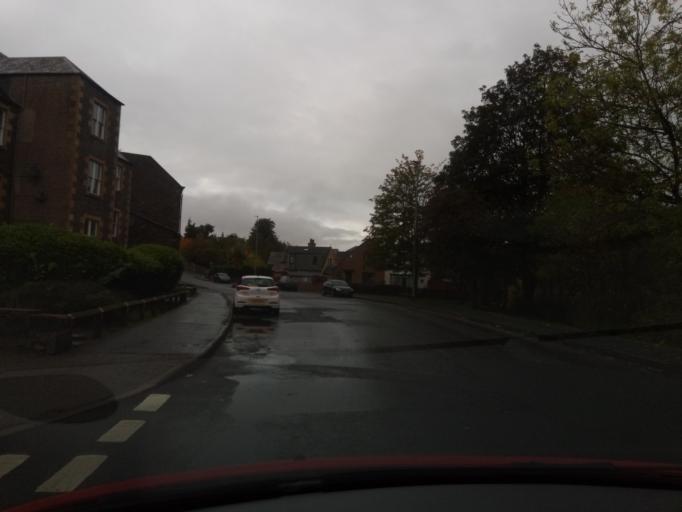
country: GB
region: Scotland
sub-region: The Scottish Borders
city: Galashiels
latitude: 55.6231
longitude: -2.8227
